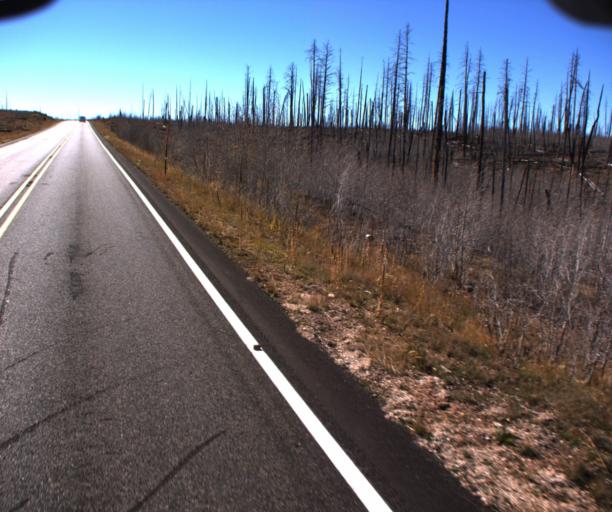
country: US
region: Arizona
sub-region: Coconino County
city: Fredonia
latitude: 36.5932
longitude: -112.1790
